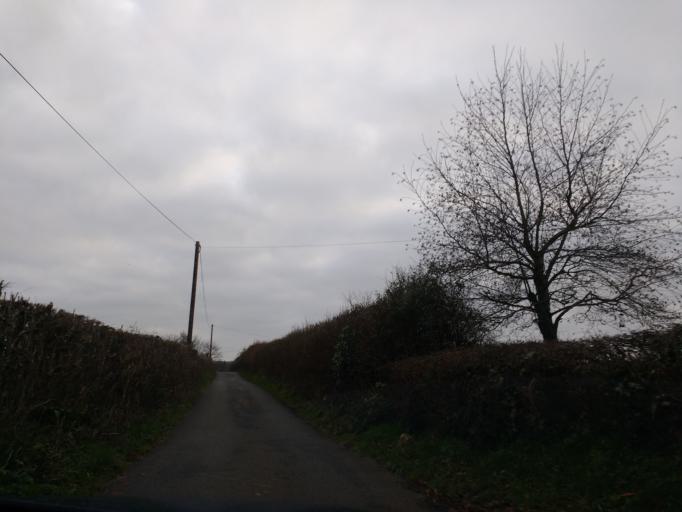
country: GB
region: England
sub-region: Isle of Wight
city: Shalfleet
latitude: 50.6890
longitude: -1.3957
